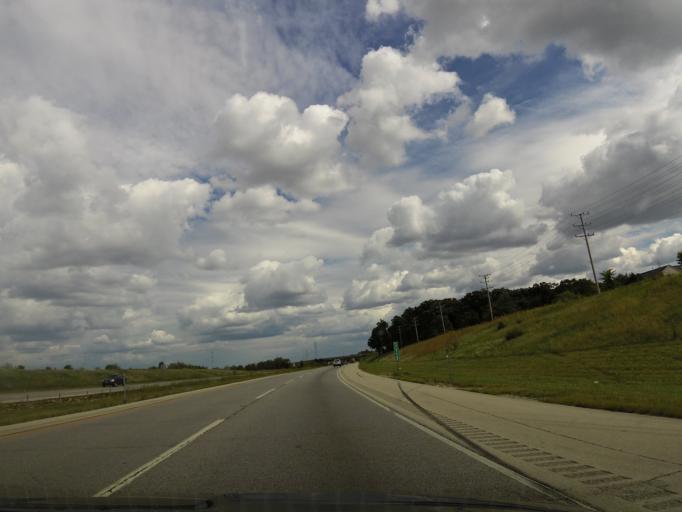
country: US
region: Illinois
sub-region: Kane County
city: Sugar Grove
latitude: 41.7987
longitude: -88.4023
